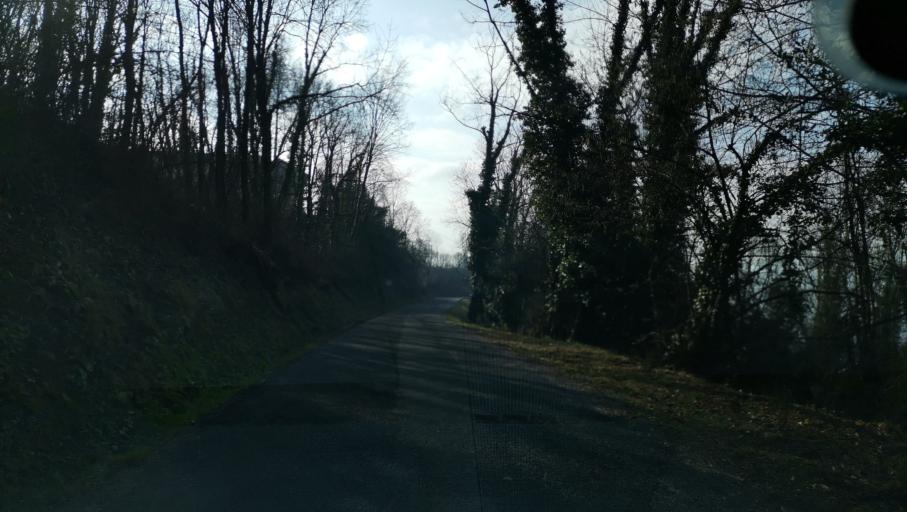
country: IT
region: Piedmont
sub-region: Provincia di Torino
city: Rivalba
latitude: 45.1364
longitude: 7.8916
